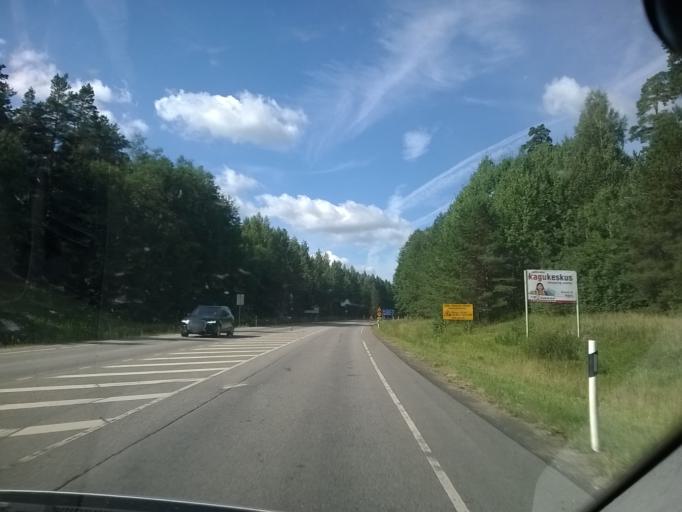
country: EE
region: Vorumaa
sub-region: Voru linn
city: Voru
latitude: 57.8180
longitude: 26.9953
